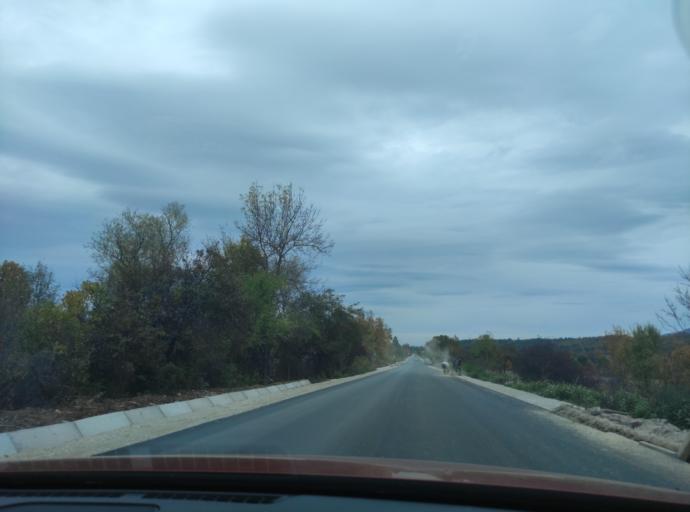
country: BG
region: Montana
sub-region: Obshtina Montana
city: Montana
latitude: 43.3729
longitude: 23.2396
